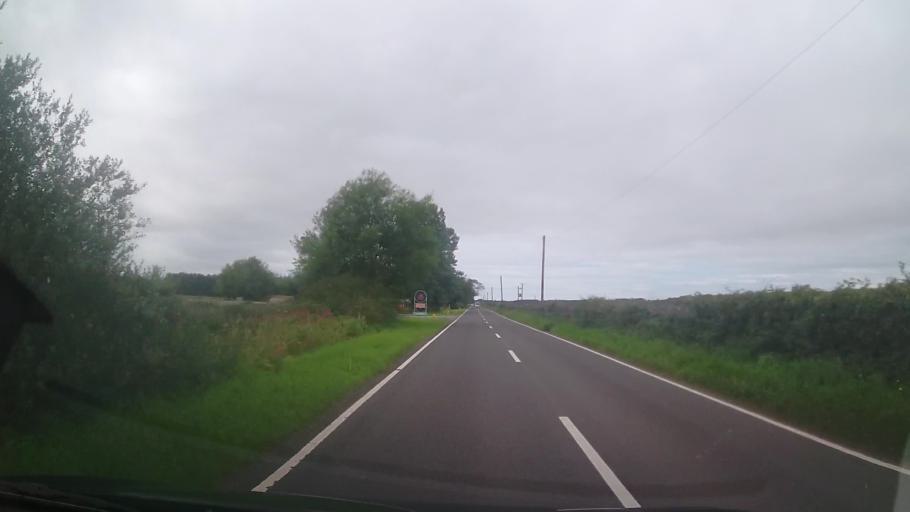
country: GB
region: Wales
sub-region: Gwynedd
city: Caernarfon
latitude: 53.1626
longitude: -4.3428
